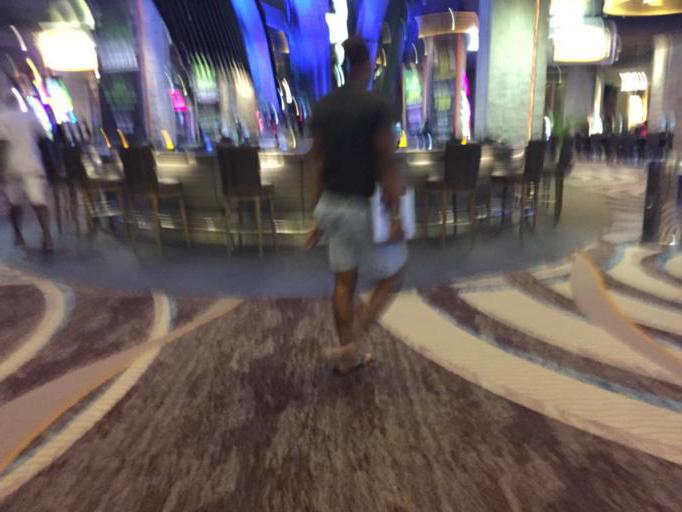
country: DO
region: San Juan
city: Punta Cana
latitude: 18.7337
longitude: -68.4824
